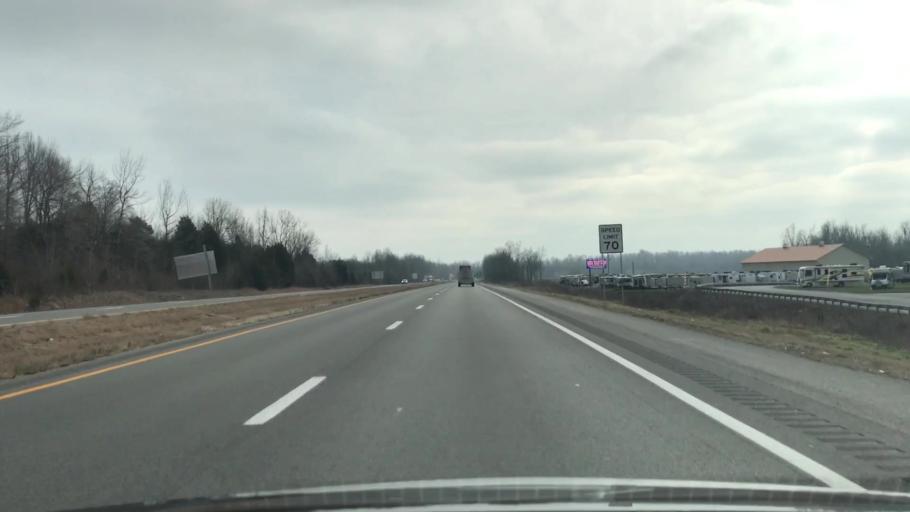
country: US
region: Kentucky
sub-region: Hopkins County
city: Madisonville
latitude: 37.3184
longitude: -87.4741
